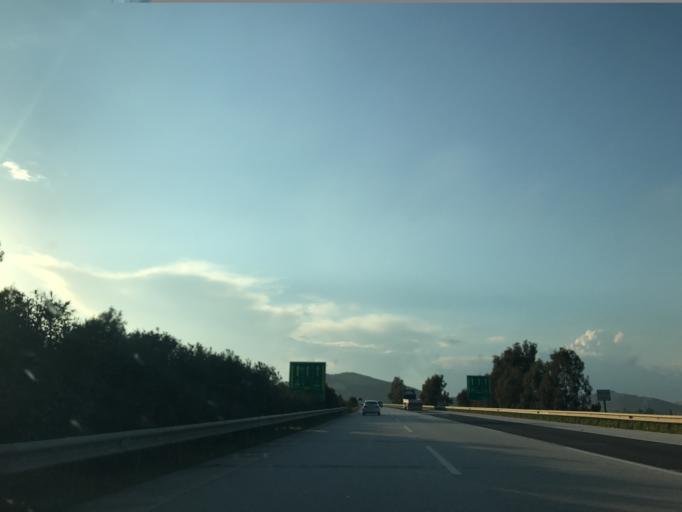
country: TR
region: Adana
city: Ceyhan
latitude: 36.9853
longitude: 35.7682
